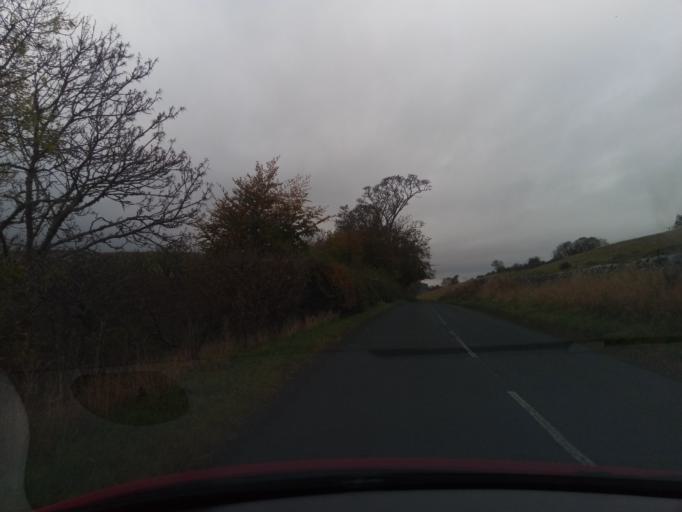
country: GB
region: Scotland
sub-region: The Scottish Borders
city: Selkirk
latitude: 55.6059
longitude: -2.8869
